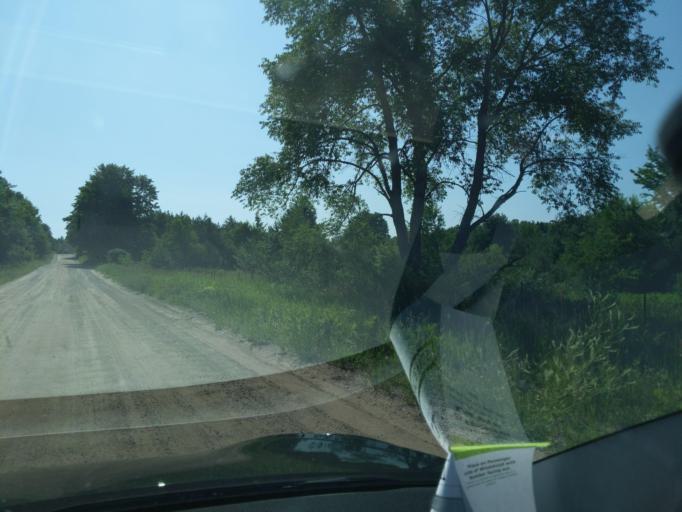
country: US
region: Michigan
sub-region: Mackinac County
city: Saint Ignace
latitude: 45.6980
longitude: -84.7224
